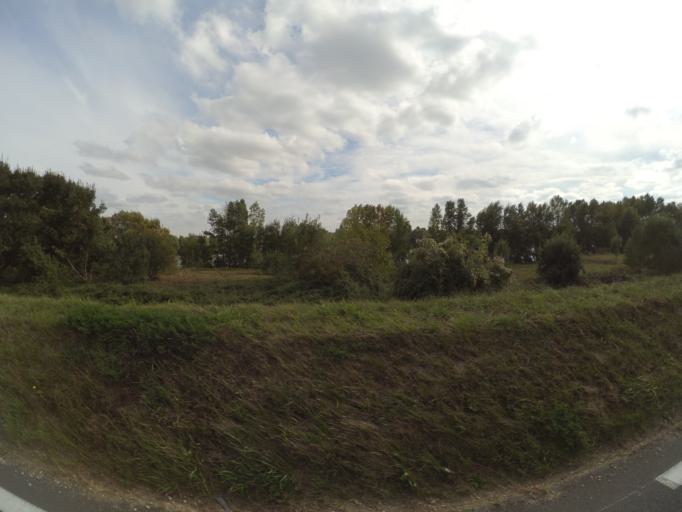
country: FR
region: Centre
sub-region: Departement d'Indre-et-Loire
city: Cinq-Mars-la-Pile
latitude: 47.3545
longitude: 0.4828
